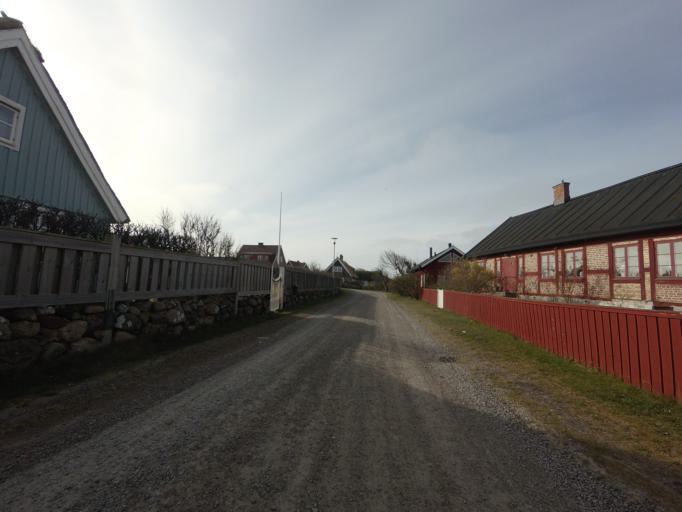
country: SE
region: Skane
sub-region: Hoganas Kommun
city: Hoganas
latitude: 56.2559
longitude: 12.5205
